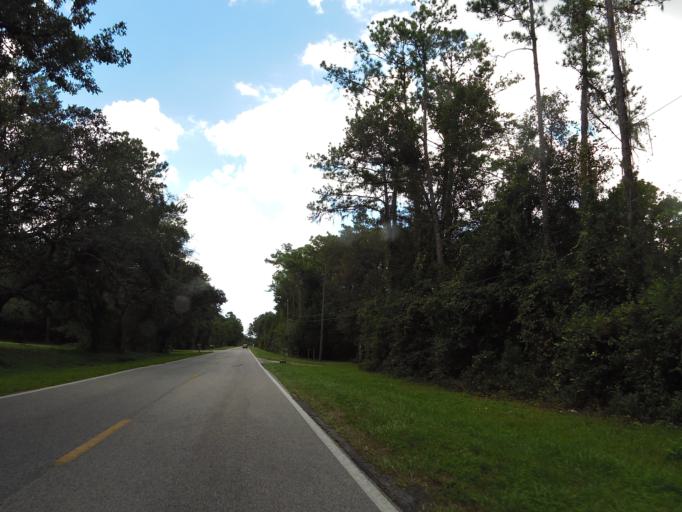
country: US
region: Florida
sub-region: Putnam County
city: East Palatka
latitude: 29.7734
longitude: -81.4822
